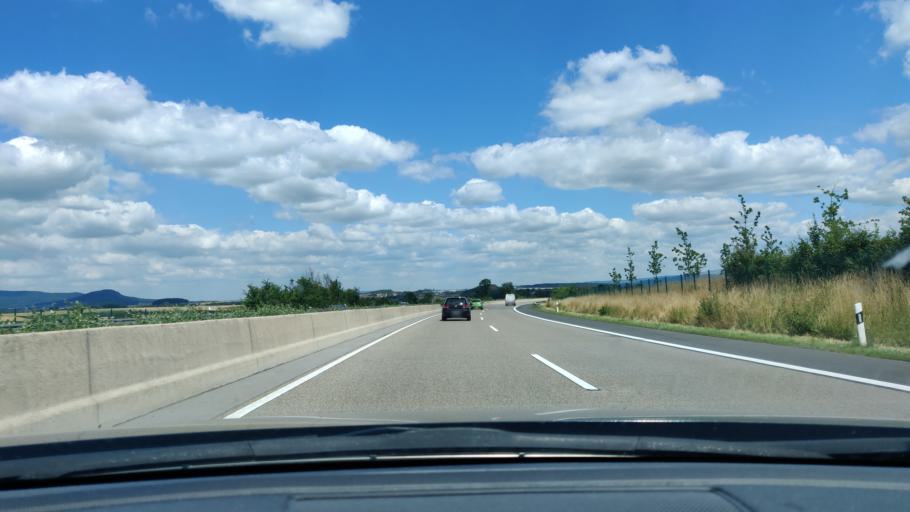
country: DE
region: Hesse
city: Gudensberg
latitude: 51.1975
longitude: 9.3996
